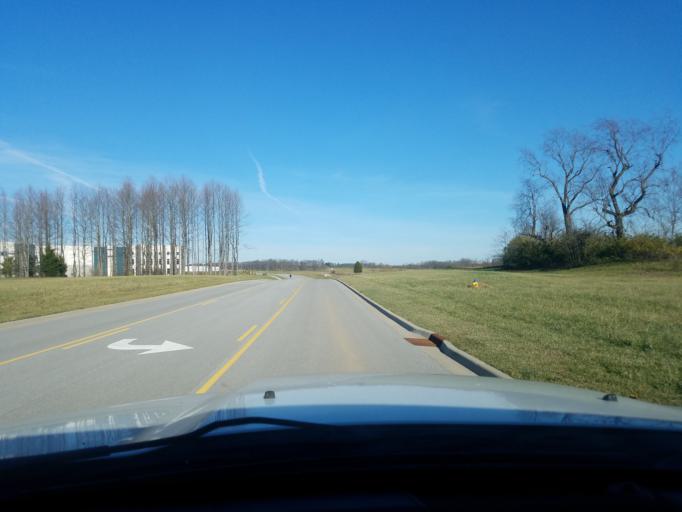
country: US
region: Indiana
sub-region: Clark County
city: Charlestown
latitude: 38.3822
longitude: -85.6795
